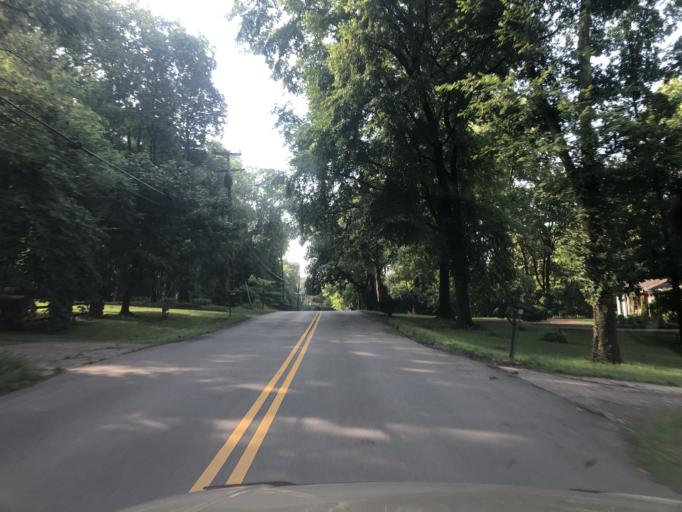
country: US
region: Tennessee
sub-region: Davidson County
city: Lakewood
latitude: 36.2270
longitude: -86.7119
